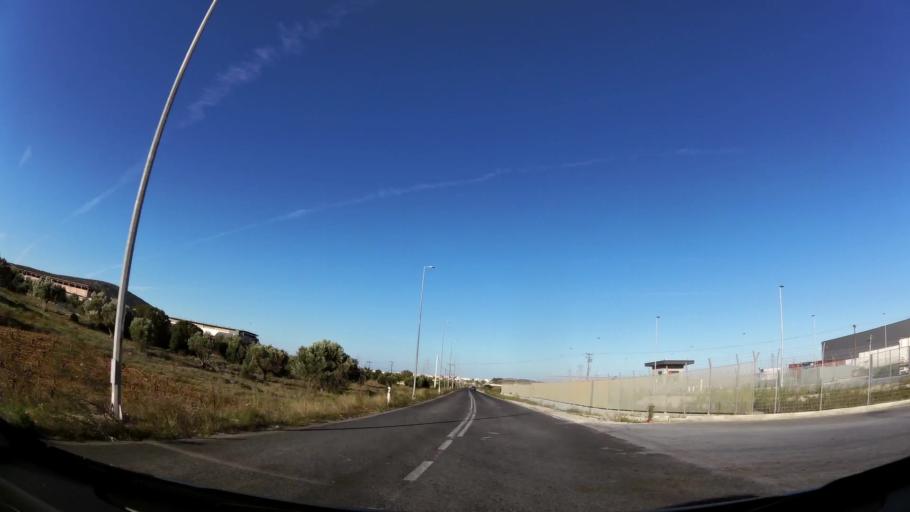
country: GR
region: Attica
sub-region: Nomarchia Anatolikis Attikis
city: Kalyvia Thorikou
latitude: 37.8584
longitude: 23.9208
